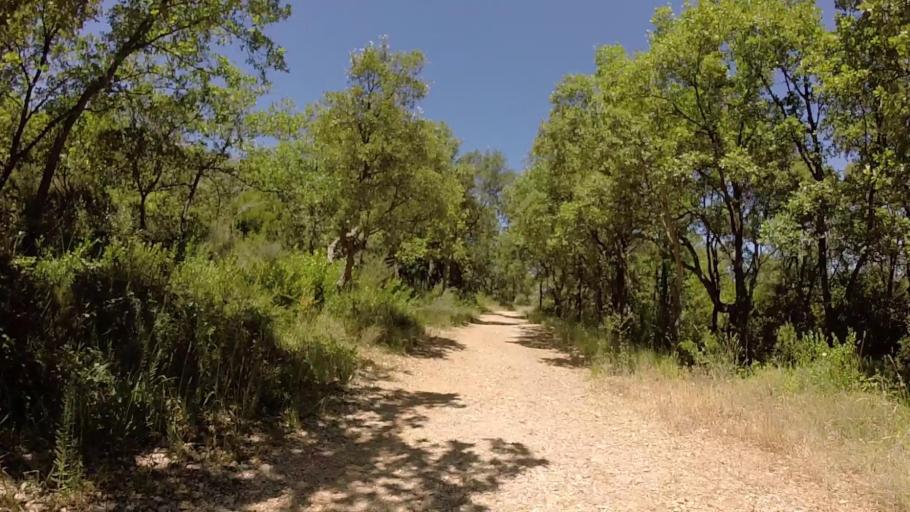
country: FR
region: Provence-Alpes-Cote d'Azur
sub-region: Departement des Alpes-Maritimes
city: Valbonne
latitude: 43.6328
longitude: 7.0328
